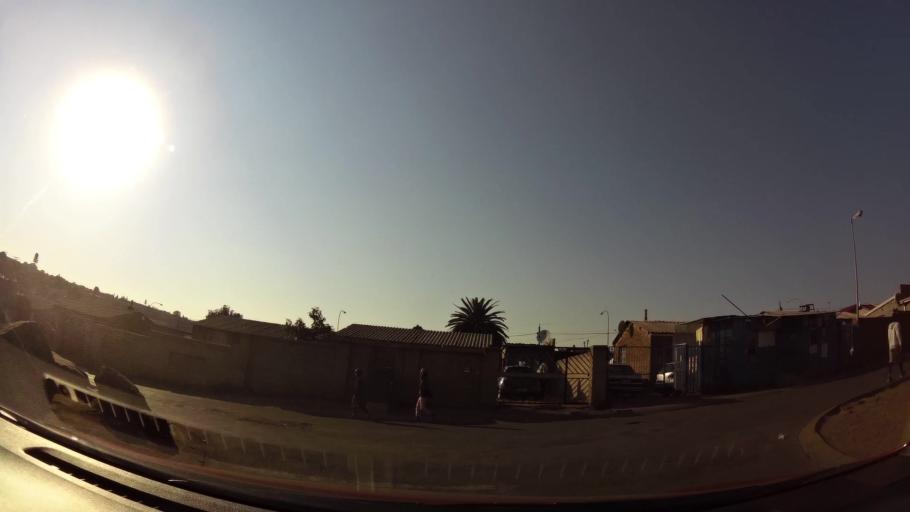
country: ZA
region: Gauteng
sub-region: City of Johannesburg Metropolitan Municipality
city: Soweto
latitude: -26.2576
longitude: 27.9511
